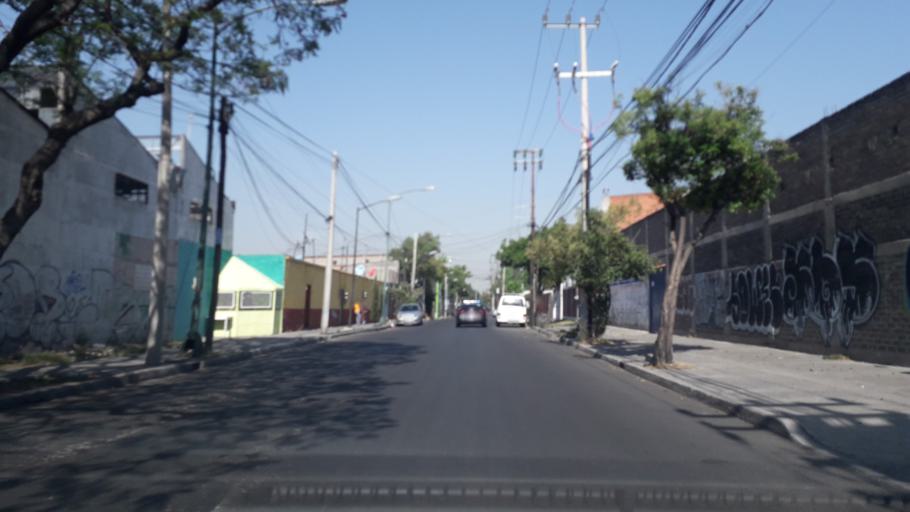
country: MX
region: Mexico City
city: Venustiano Carranza
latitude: 19.4236
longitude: -99.0918
